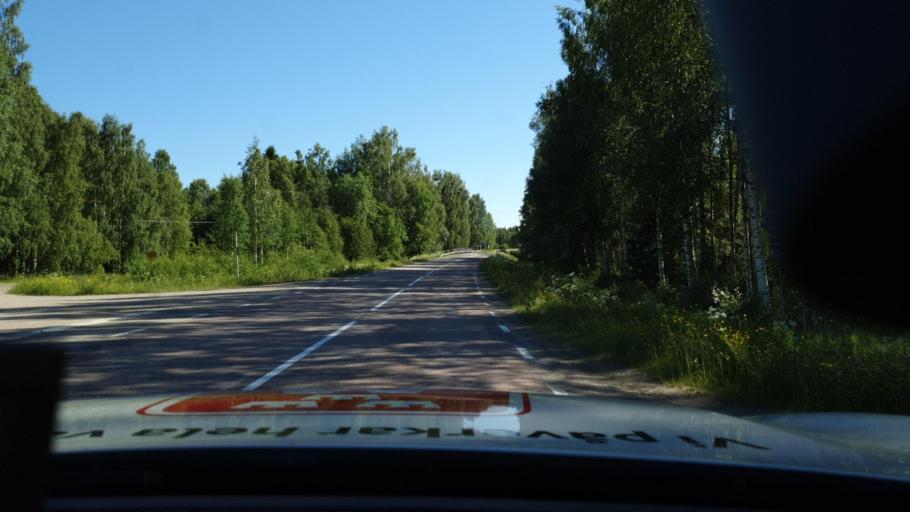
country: SE
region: Norrbotten
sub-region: Lulea Kommun
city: Ranea
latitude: 65.9520
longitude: 22.3971
